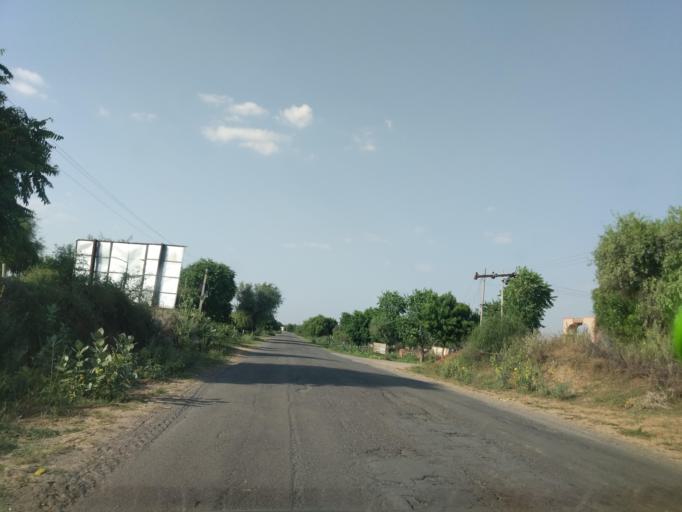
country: IN
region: Rajasthan
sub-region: Churu
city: Rajgarh
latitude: 28.5161
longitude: 75.3832
